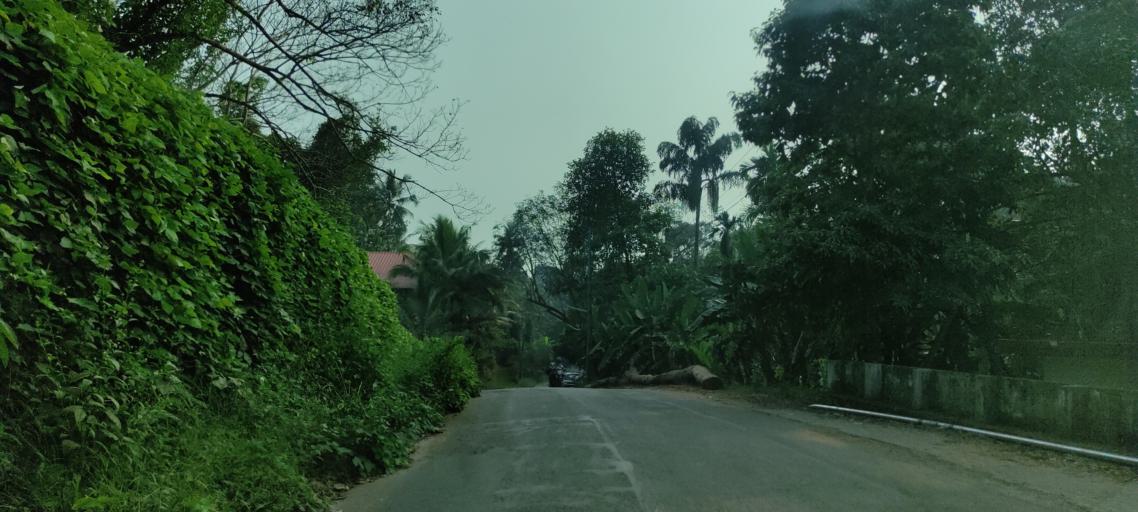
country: IN
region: Kerala
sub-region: Ernakulam
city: Piravam
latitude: 9.7821
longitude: 76.4983
